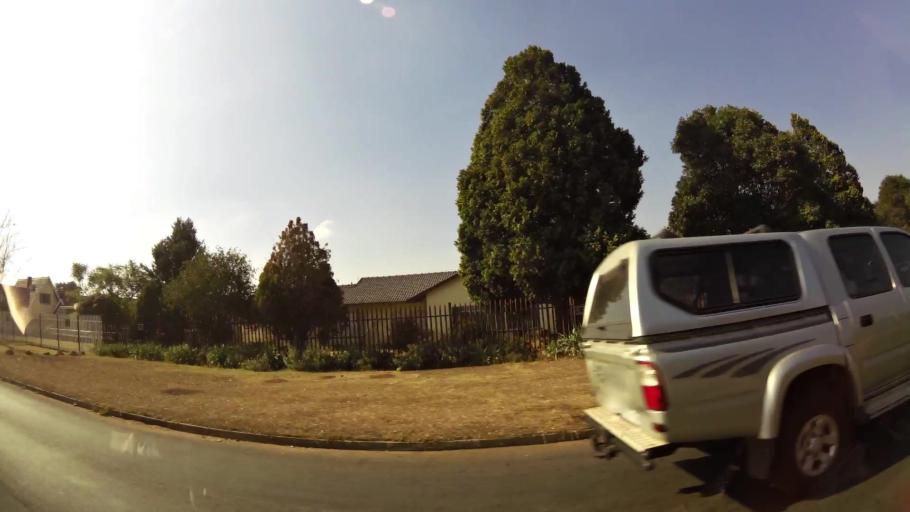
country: ZA
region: Gauteng
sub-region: West Rand District Municipality
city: Randfontein
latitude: -26.1582
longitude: 27.7021
